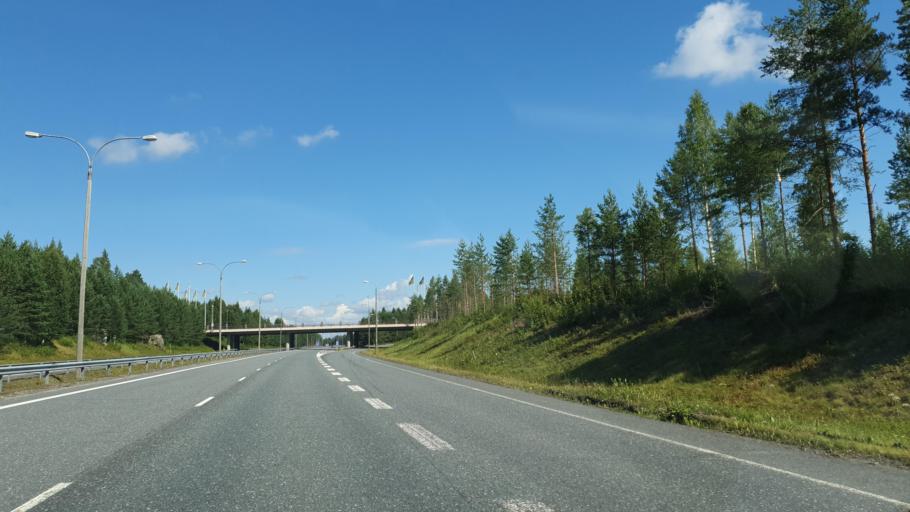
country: FI
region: Northern Savo
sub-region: Ylae-Savo
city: Iisalmi
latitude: 63.5440
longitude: 27.2493
